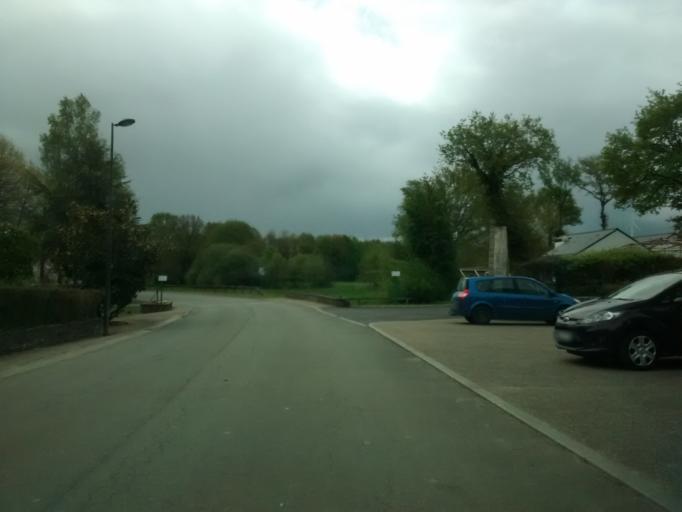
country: FR
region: Brittany
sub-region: Departement du Morbihan
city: Ruffiac
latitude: 47.7941
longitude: -2.3193
